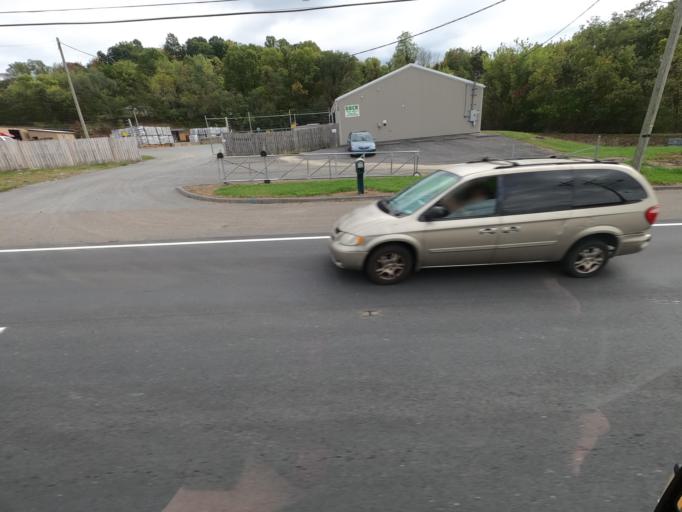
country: US
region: Tennessee
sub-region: Washington County
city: Johnson City
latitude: 36.3264
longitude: -82.3278
